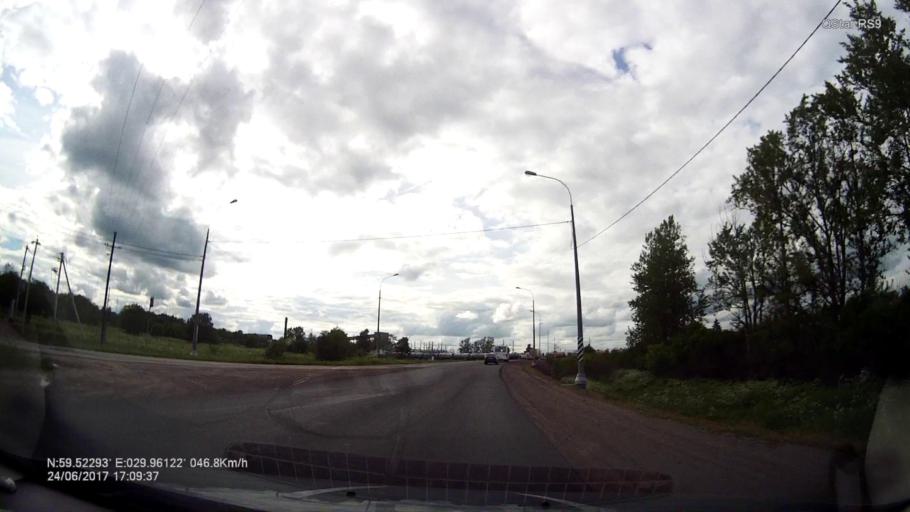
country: RU
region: Leningrad
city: Voyskovitsy
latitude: 59.5231
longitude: 29.9607
